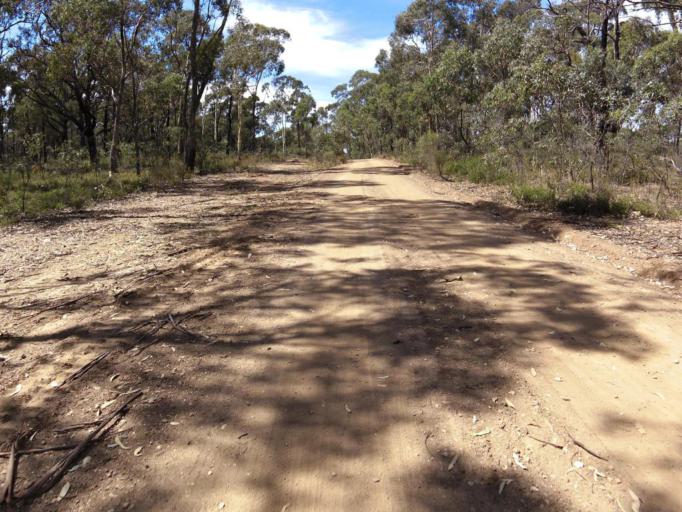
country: AU
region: Victoria
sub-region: Greater Bendigo
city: White Hills
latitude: -36.7578
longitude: 144.3316
